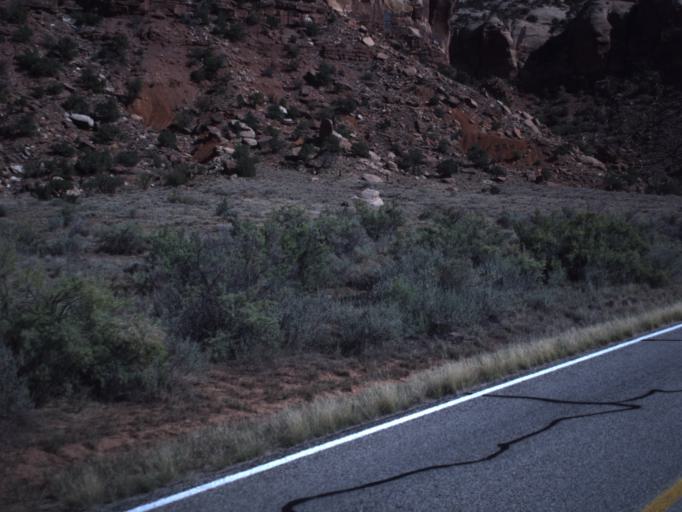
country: US
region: Utah
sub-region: San Juan County
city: Monticello
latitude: 38.0524
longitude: -109.5528
